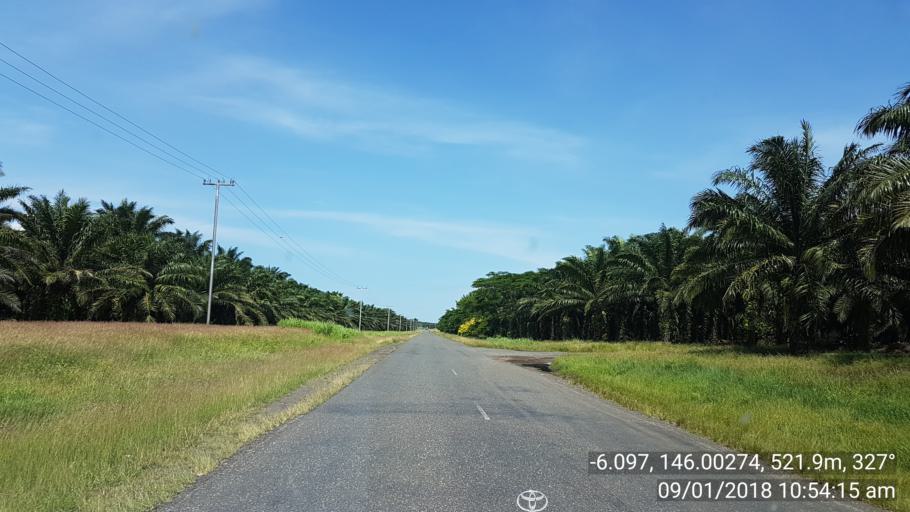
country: PG
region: Eastern Highlands
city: Kainantu
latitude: -6.0972
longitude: 146.0028
